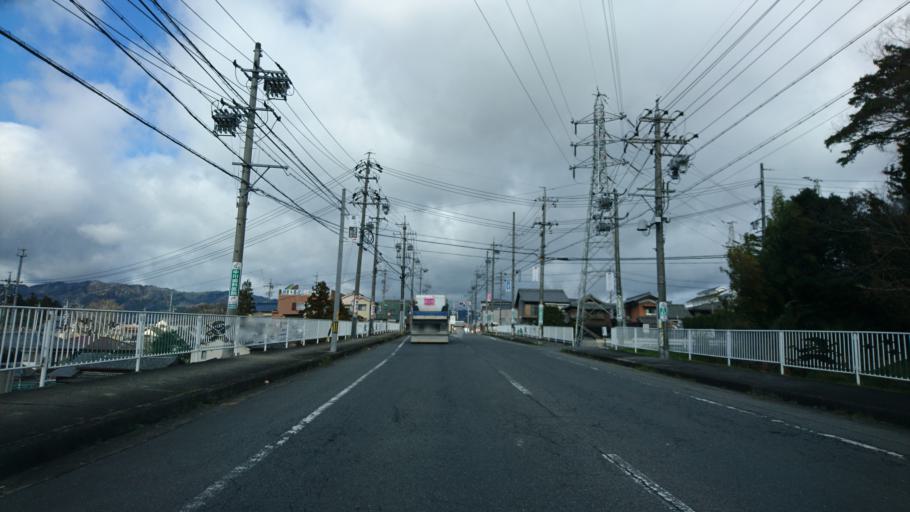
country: JP
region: Mie
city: Ueno-ebisumachi
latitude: 34.7643
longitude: 136.1234
